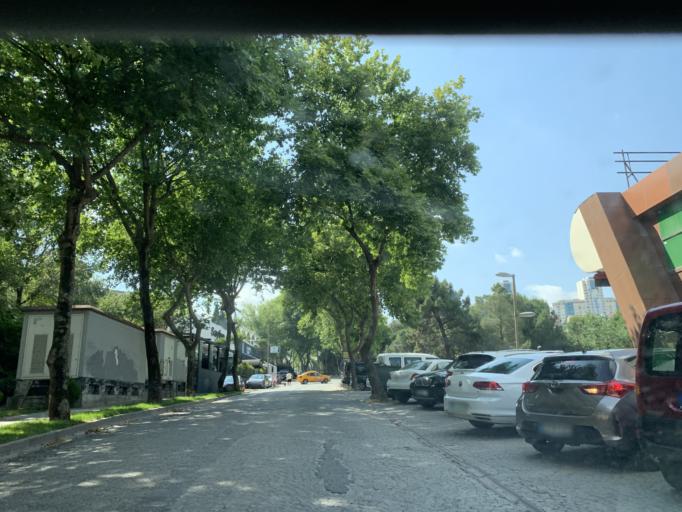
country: TR
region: Istanbul
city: Esenyurt
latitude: 41.0677
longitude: 28.6903
